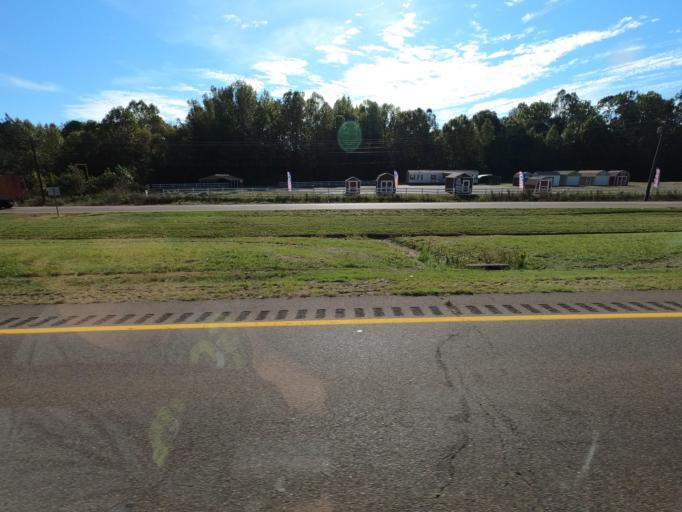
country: US
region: Tennessee
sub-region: Tipton County
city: Atoka
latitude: 35.4565
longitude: -89.7733
